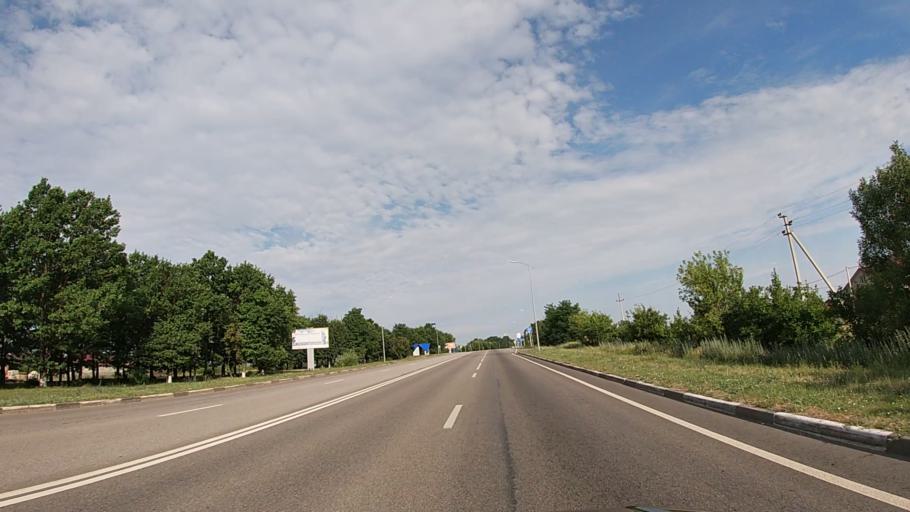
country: RU
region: Belgorod
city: Severnyy
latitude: 50.6376
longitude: 36.4463
